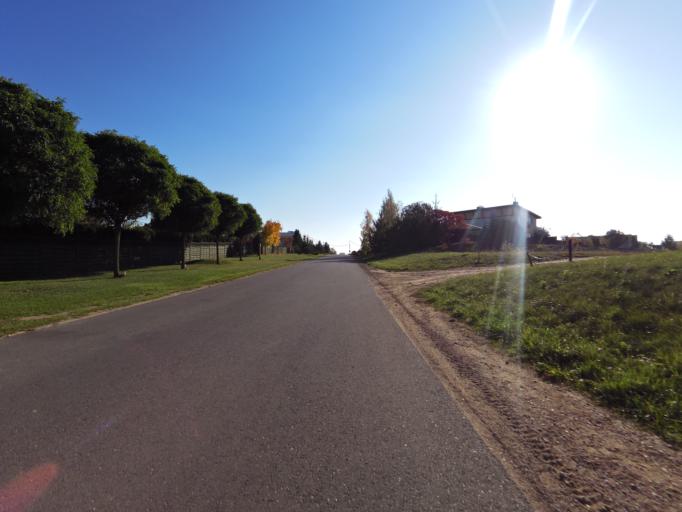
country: LT
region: Vilnius County
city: Pasilaiciai
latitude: 54.7306
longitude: 25.2059
